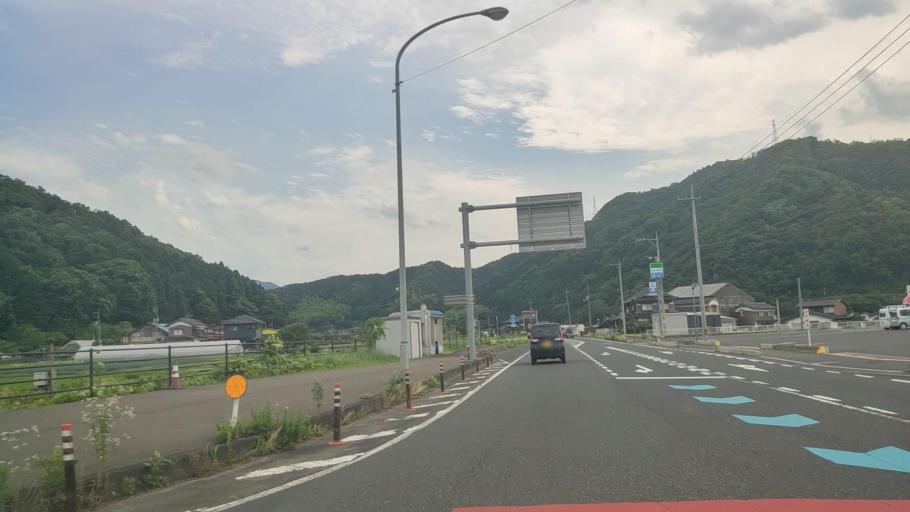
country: JP
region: Tottori
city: Tottori
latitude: 35.3539
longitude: 134.2057
